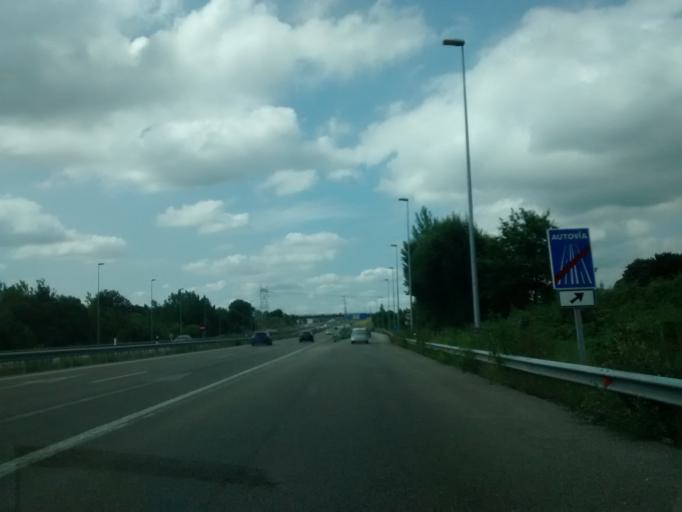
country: ES
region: Asturias
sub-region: Province of Asturias
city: Pola de Siero
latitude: 43.3768
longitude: -5.6846
